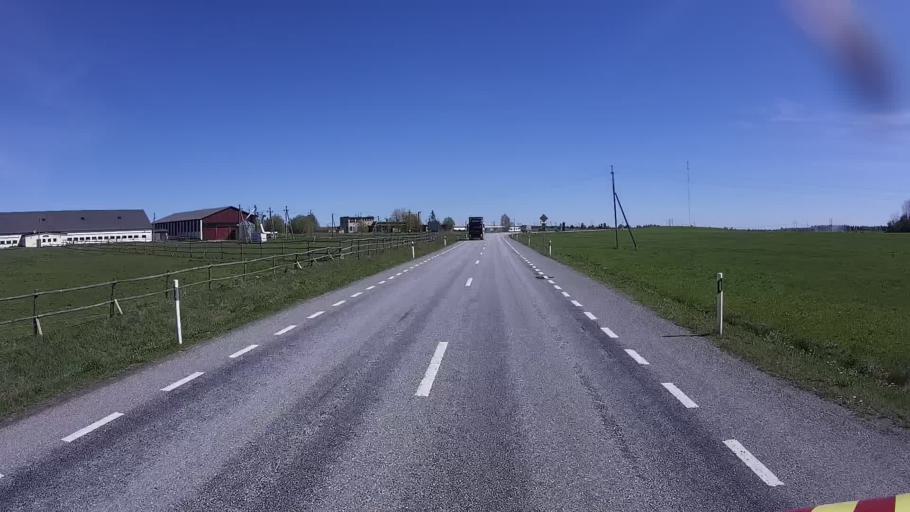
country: EE
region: Laeaene-Virumaa
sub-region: Tapa vald
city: Tapa
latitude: 59.2449
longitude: 25.6906
